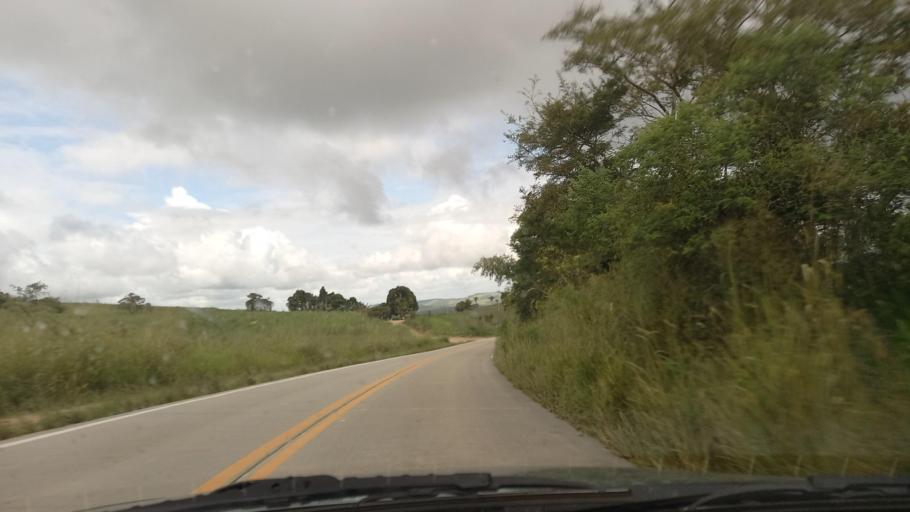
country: BR
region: Pernambuco
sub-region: Quipapa
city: Quipapa
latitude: -8.7891
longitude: -35.9902
